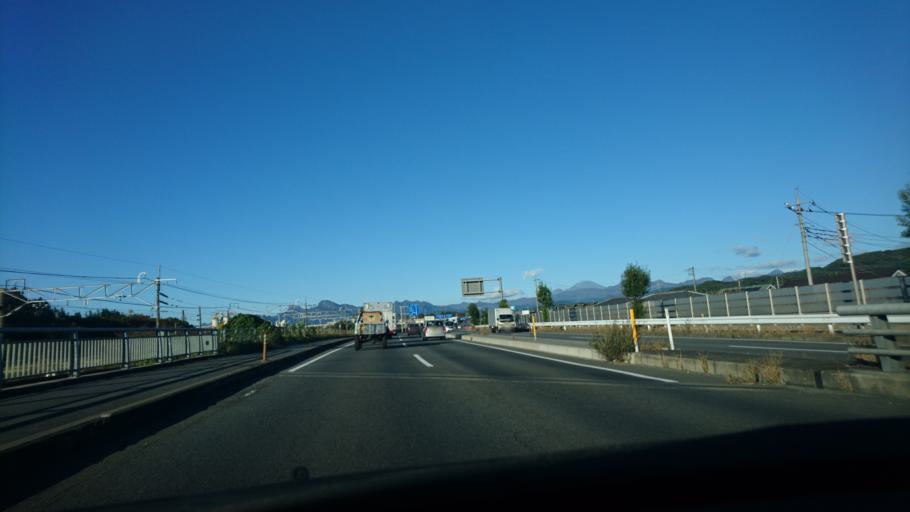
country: JP
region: Gunma
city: Annaka
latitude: 36.3320
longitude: 138.9206
